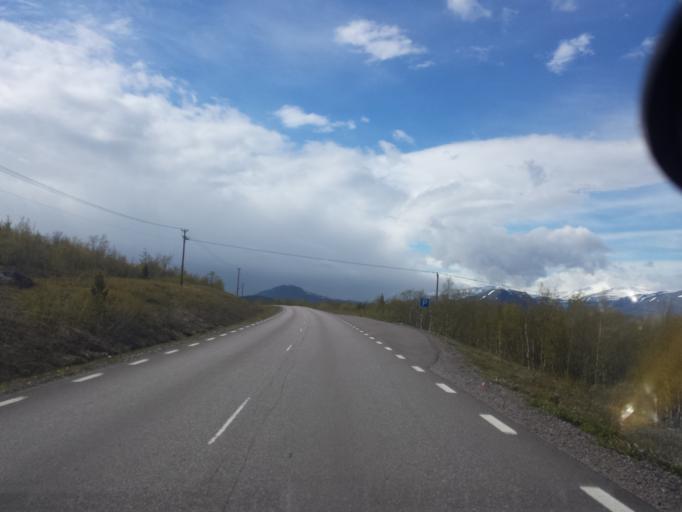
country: SE
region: Norrbotten
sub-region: Kiruna Kommun
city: Kiruna
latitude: 68.2150
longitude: 19.7413
